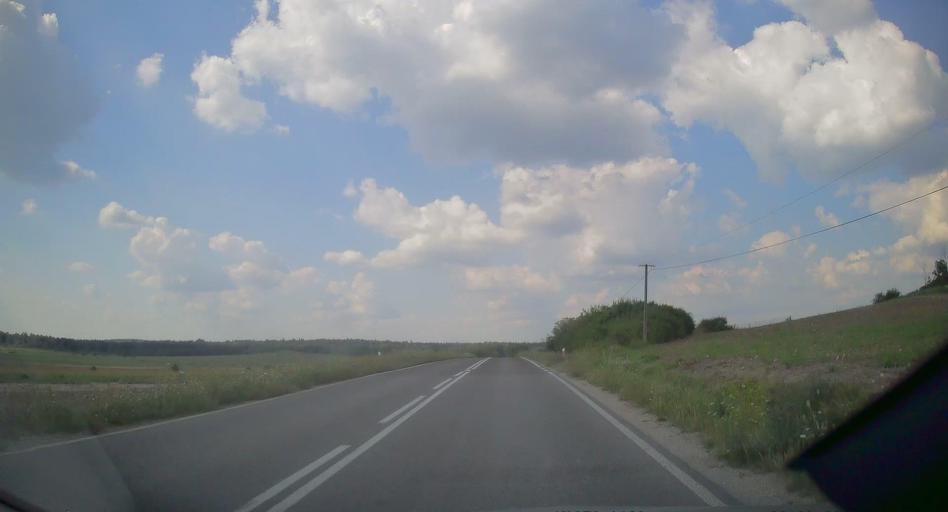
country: PL
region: Swietokrzyskie
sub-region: Powiat jedrzejowski
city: Malogoszcz
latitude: 50.8731
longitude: 20.2683
